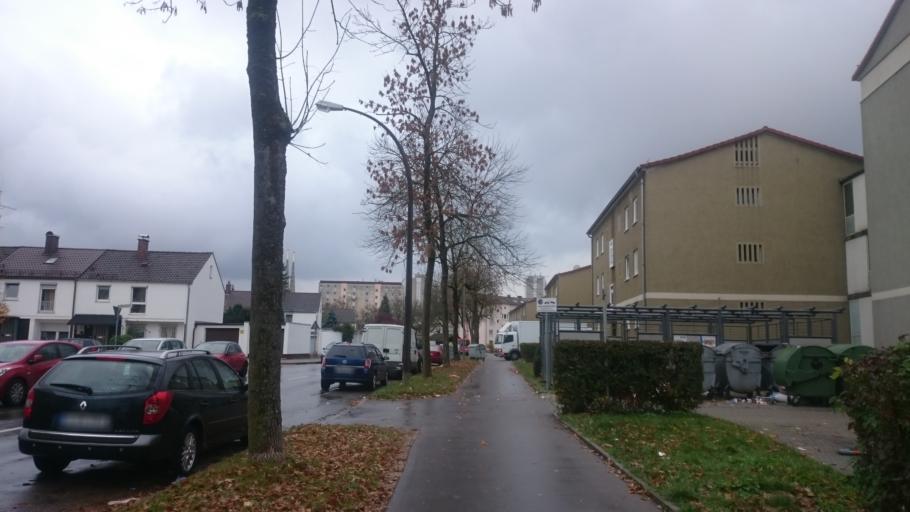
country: DE
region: Bavaria
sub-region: Swabia
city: Augsburg
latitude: 48.3617
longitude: 10.9229
